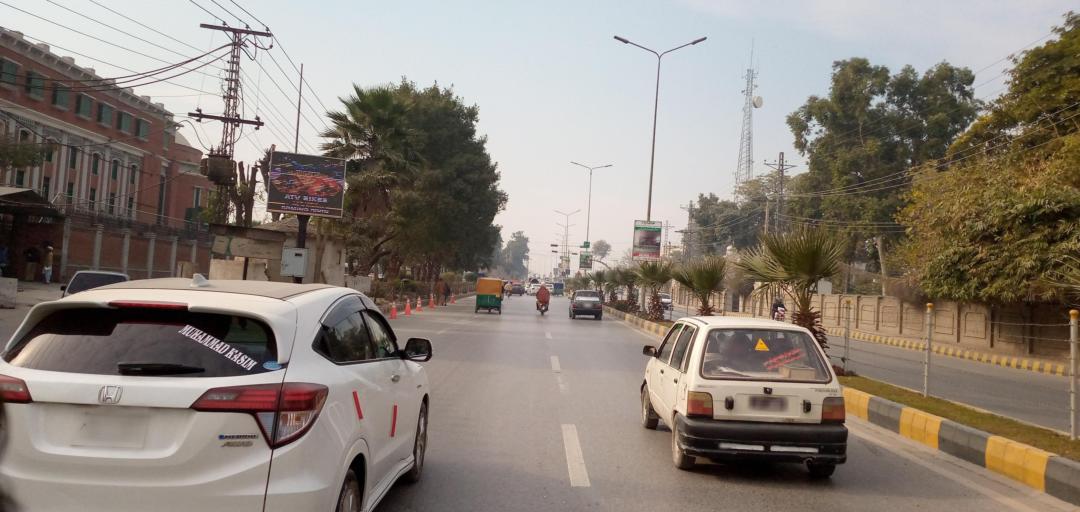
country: PK
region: Khyber Pakhtunkhwa
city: Peshawar
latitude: 34.0146
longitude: 71.5575
